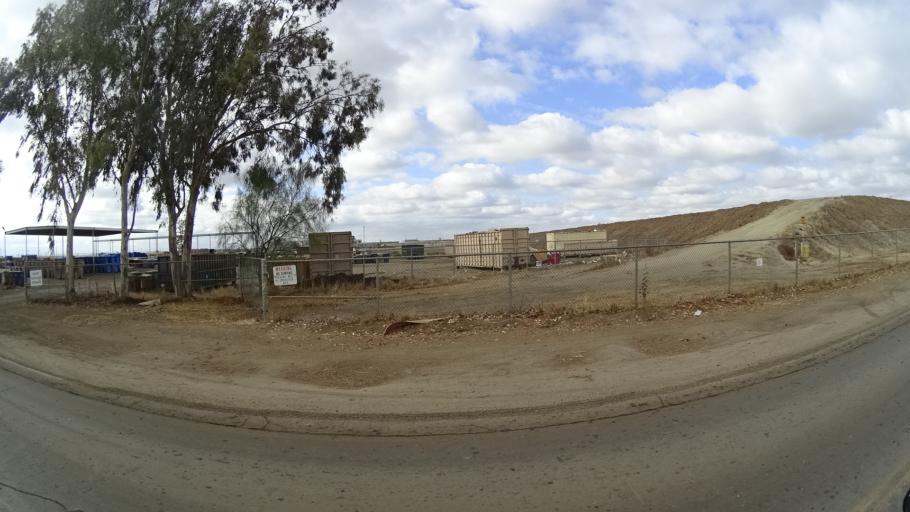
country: US
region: California
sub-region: Kern County
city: Greenfield
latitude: 35.3271
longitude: -118.9676
